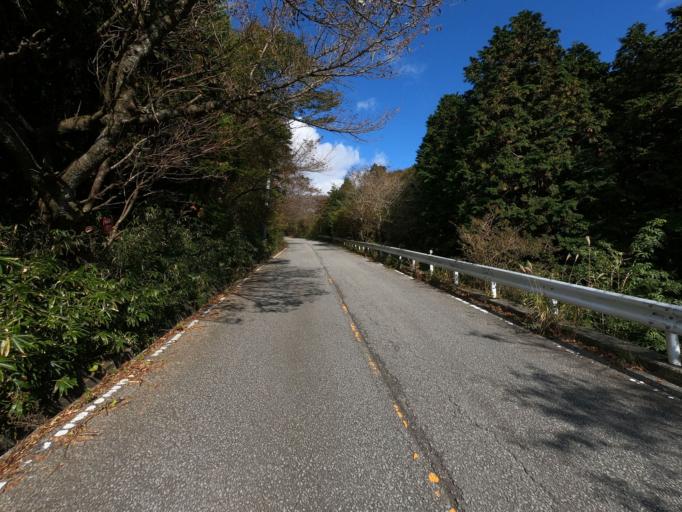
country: JP
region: Kanagawa
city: Hakone
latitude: 35.1820
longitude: 139.0612
